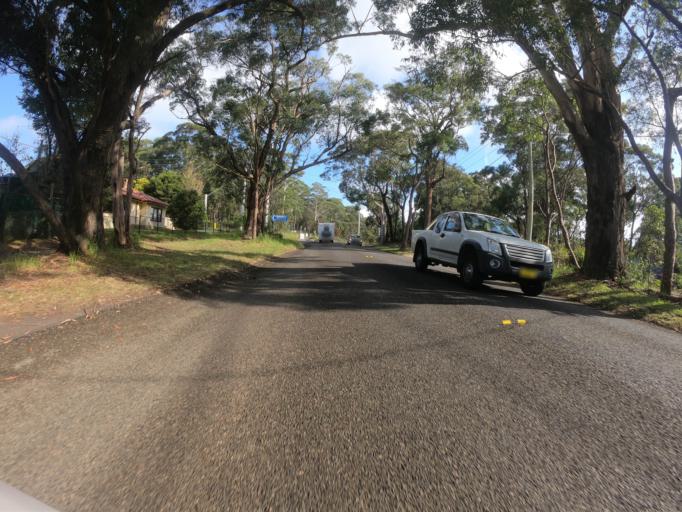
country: AU
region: New South Wales
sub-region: Wollongong
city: Helensburgh
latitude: -34.1970
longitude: 150.9743
